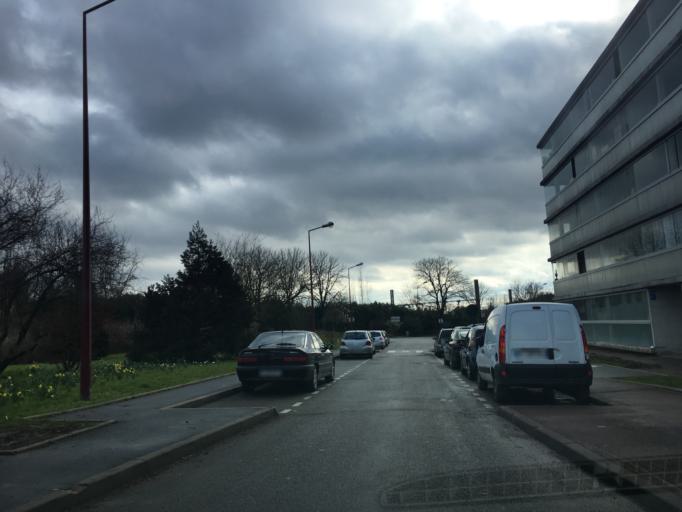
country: FR
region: Ile-de-France
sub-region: Departement du Val-d'Oise
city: Arnouville
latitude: 49.0025
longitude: 2.4280
